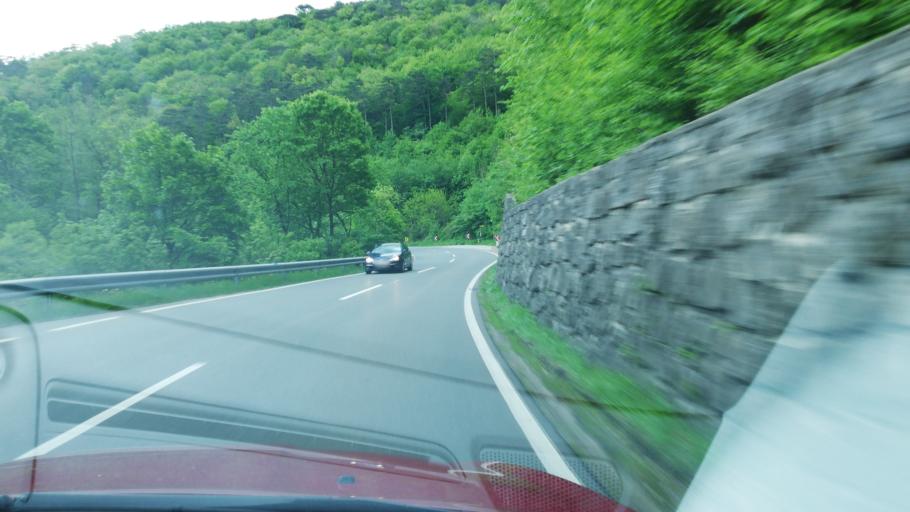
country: AT
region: Lower Austria
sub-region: Politischer Bezirk Modling
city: Gaaden
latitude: 48.0193
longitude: 16.1670
